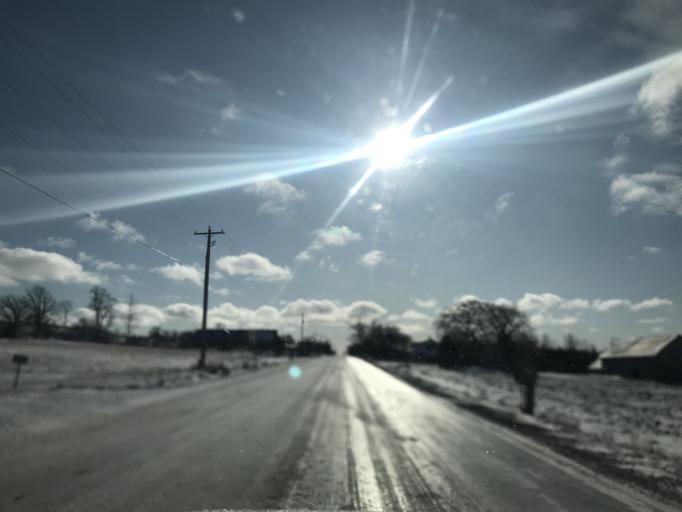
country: US
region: Wisconsin
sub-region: Kewaunee County
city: Luxemburg
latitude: 44.7106
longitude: -87.6207
